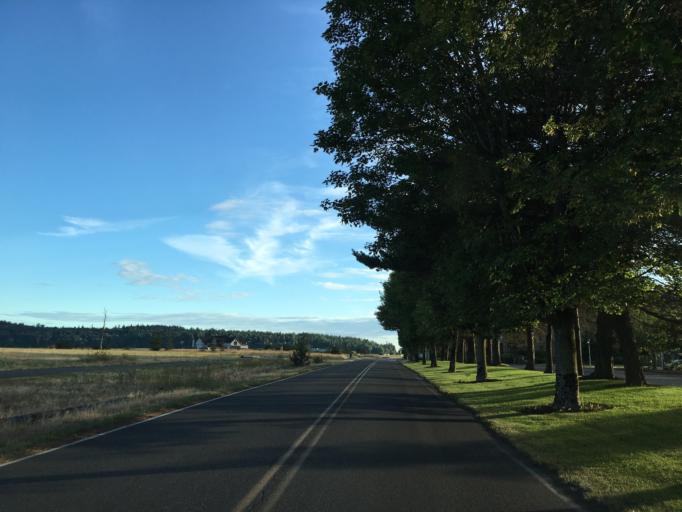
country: US
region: Washington
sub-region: Whatcom County
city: Blaine
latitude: 48.9891
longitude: -122.7740
